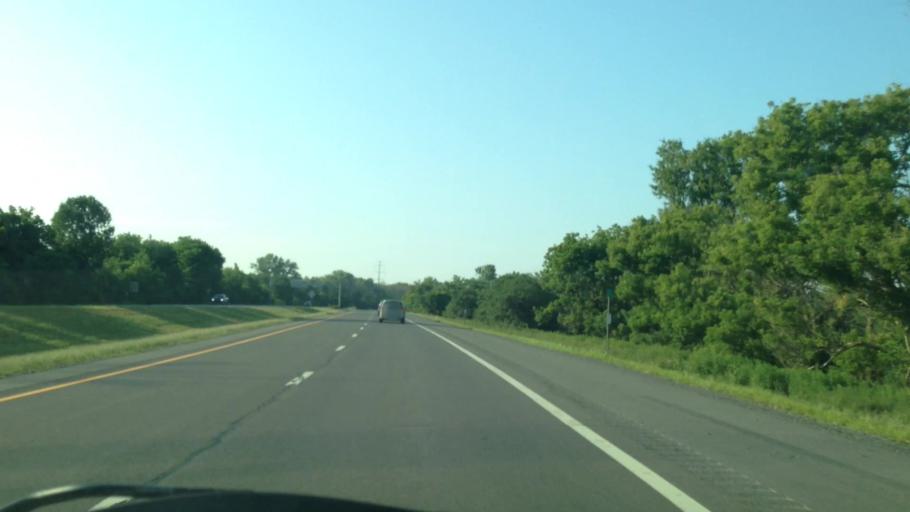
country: US
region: New York
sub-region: Onondaga County
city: East Syracuse
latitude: 43.0237
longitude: -76.0619
